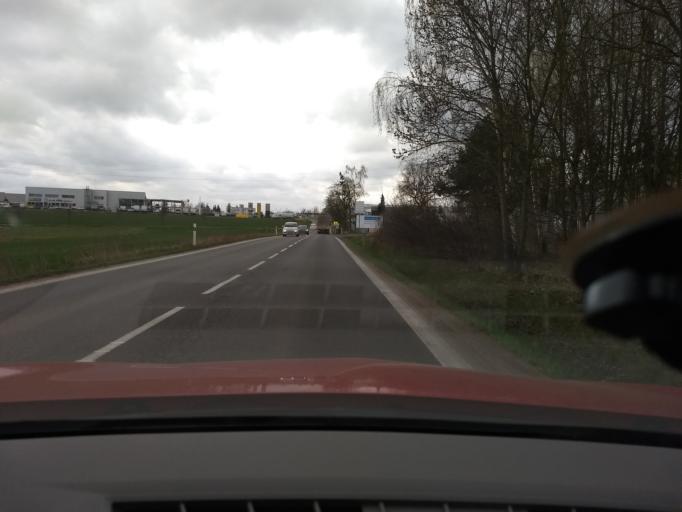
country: CZ
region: Central Bohemia
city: Kladno
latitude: 50.1244
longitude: 14.1270
